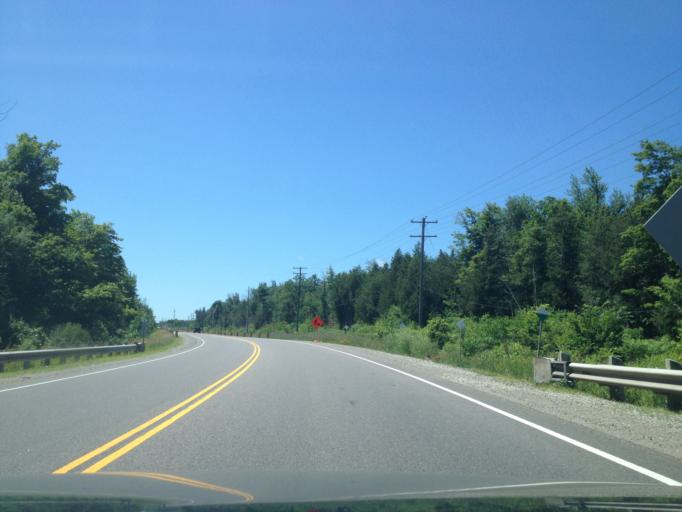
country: CA
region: Ontario
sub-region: Halton
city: Milton
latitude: 43.6730
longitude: -79.9883
